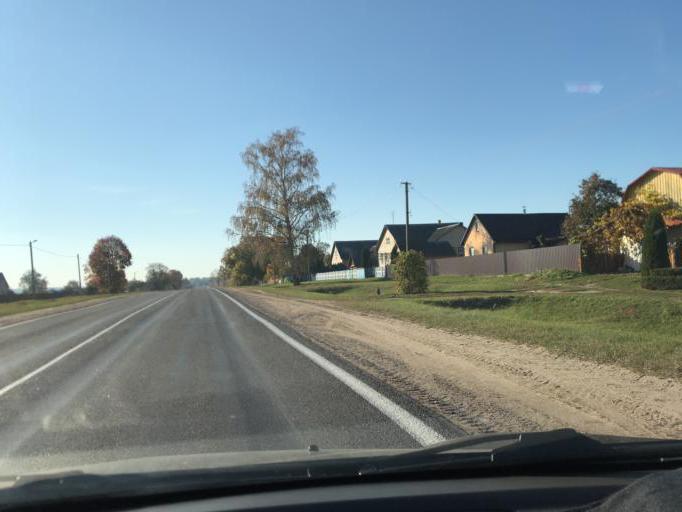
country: BY
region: Minsk
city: Staryya Darohi
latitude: 53.0545
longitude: 28.4162
